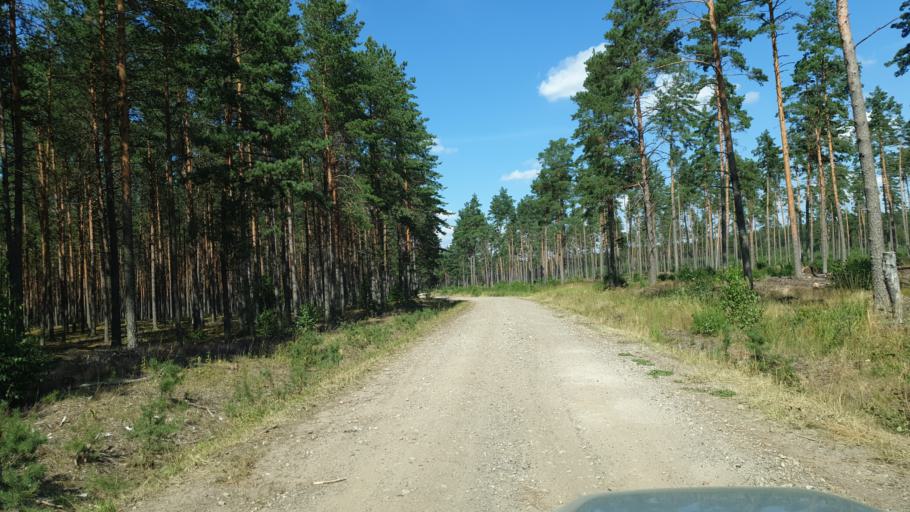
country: LT
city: Sirvintos
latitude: 54.8972
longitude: 24.9573
